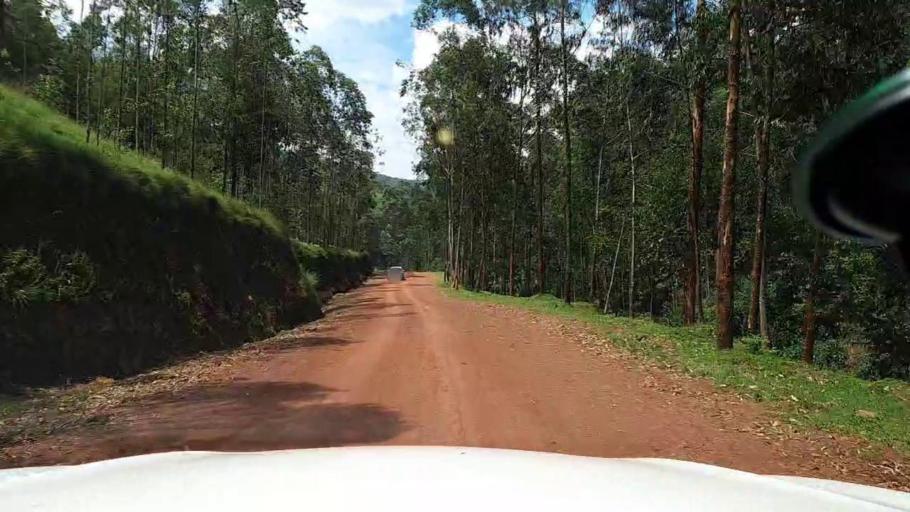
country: RW
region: Northern Province
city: Byumba
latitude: -1.7047
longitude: 29.8462
